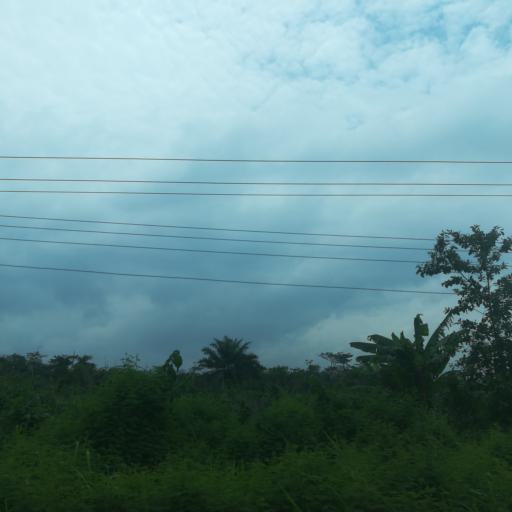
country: NG
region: Lagos
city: Ejirin
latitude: 6.6476
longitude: 3.7805
